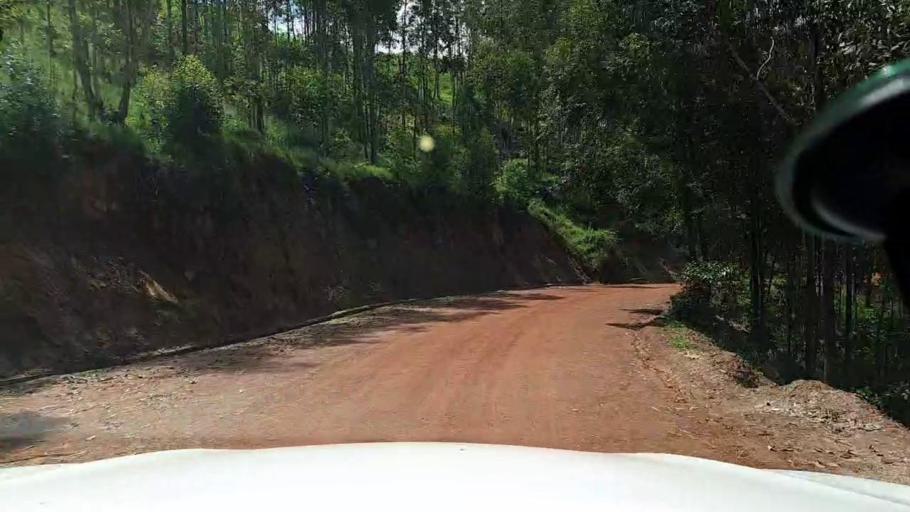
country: RW
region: Northern Province
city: Byumba
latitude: -1.6902
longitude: 29.8247
